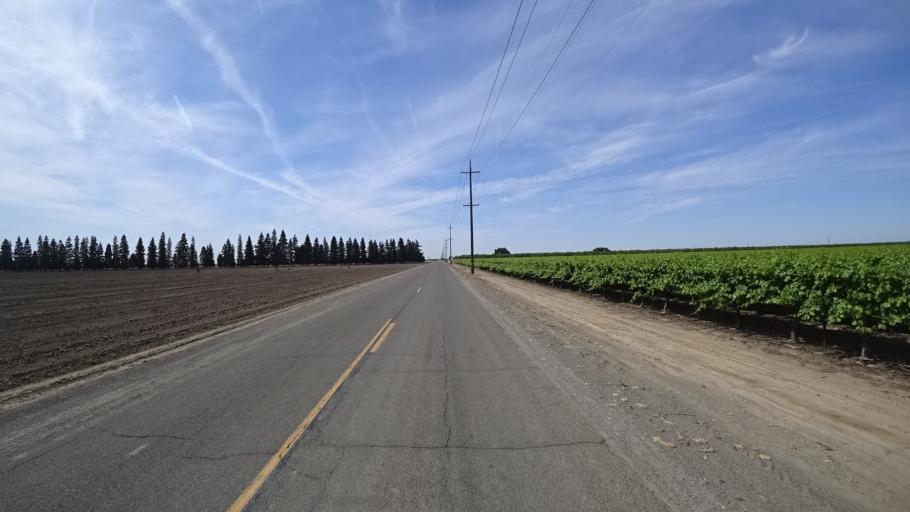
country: US
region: California
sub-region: Kings County
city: Lucerne
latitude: 36.4149
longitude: -119.5830
